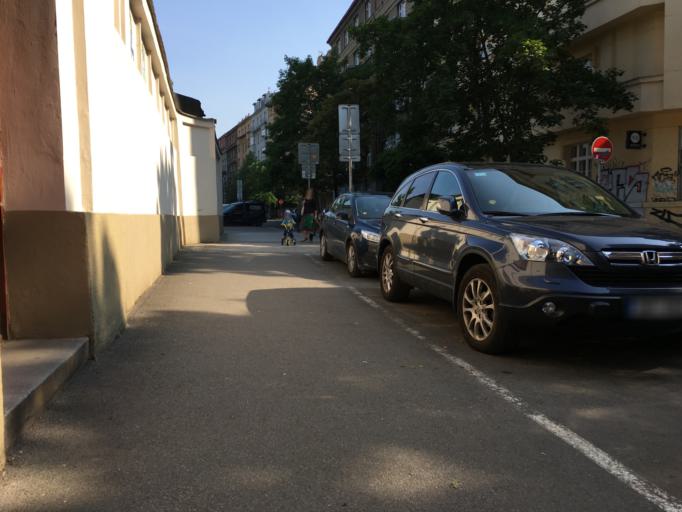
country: CZ
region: Praha
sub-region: Praha 8
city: Karlin
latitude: 50.0815
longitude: 14.4494
